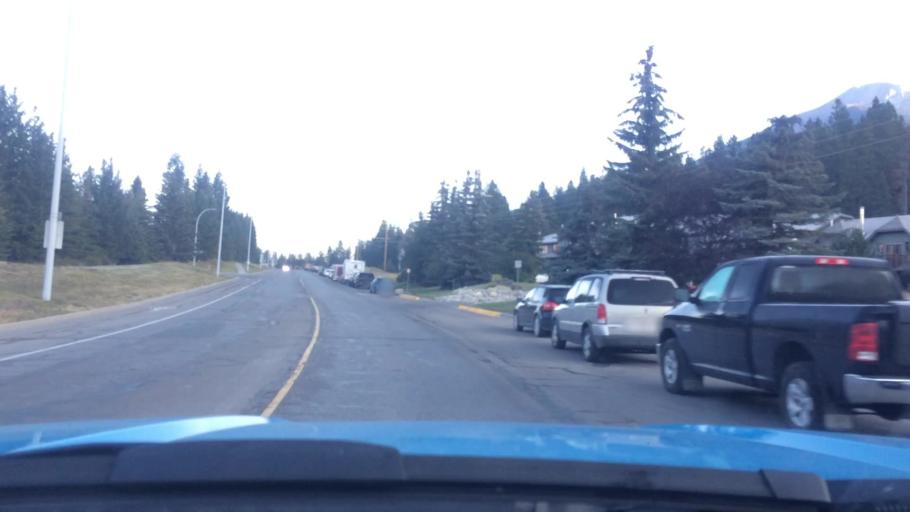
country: CA
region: Alberta
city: Canmore
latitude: 51.0813
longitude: -115.3216
